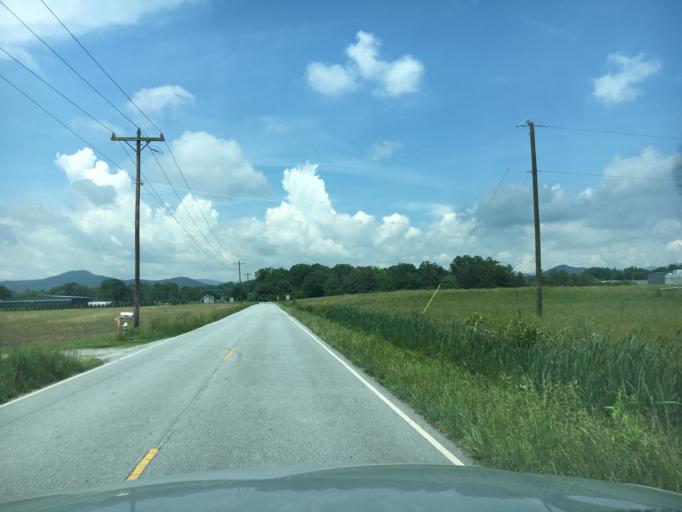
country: US
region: North Carolina
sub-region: Henderson County
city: Mills River
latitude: 35.3776
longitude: -82.5541
